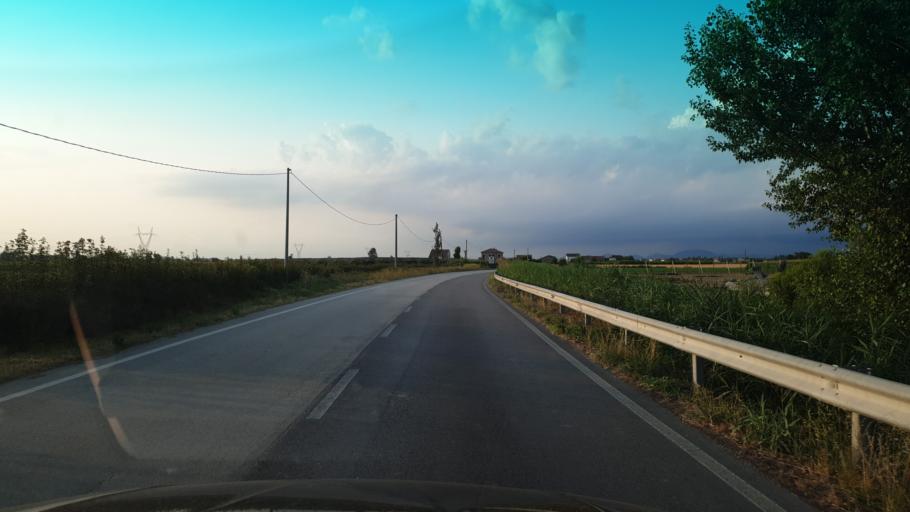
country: IT
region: Veneto
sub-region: Provincia di Rovigo
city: San Bellino
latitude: 45.0519
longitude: 11.5813
